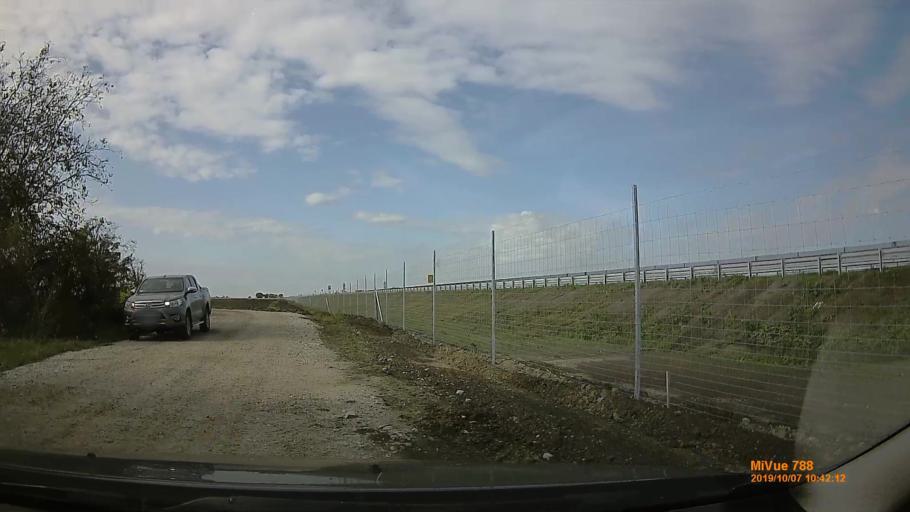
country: HU
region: Bekes
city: Kondoros
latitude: 46.7451
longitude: 20.8436
